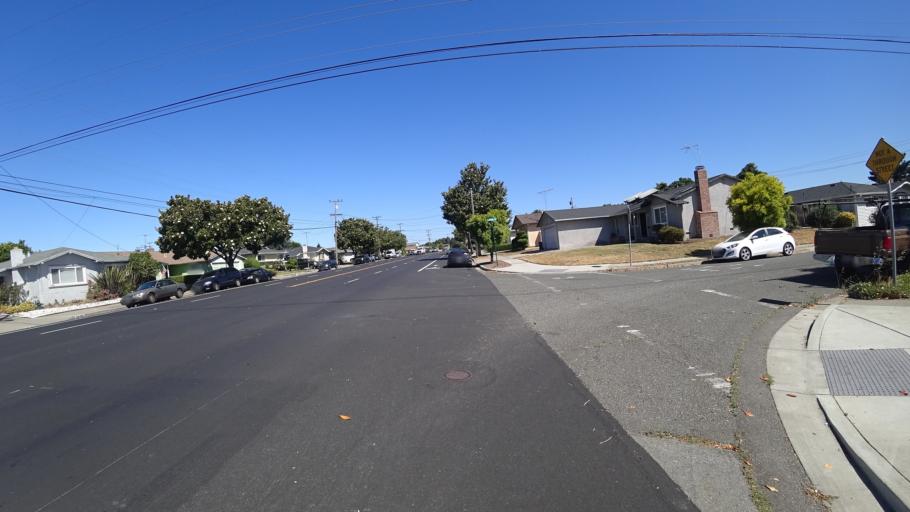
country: US
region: California
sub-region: Alameda County
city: Hayward
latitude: 37.6514
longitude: -122.0936
